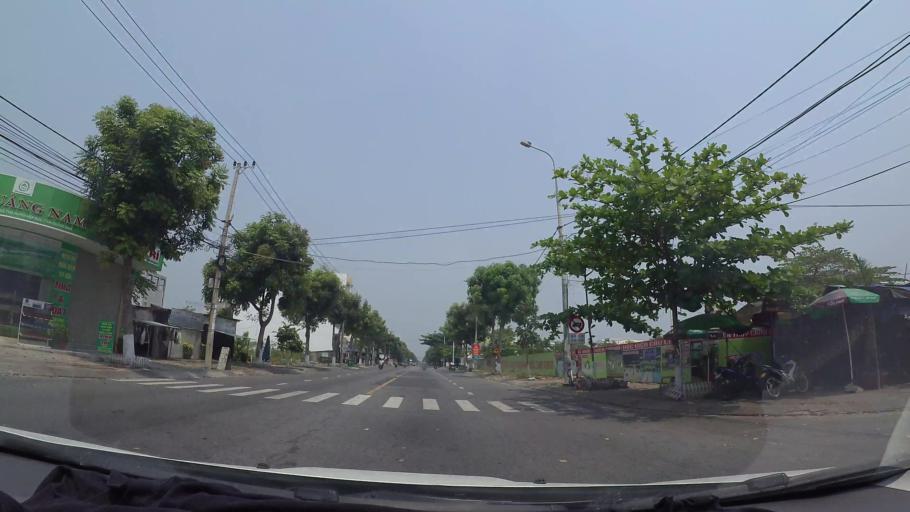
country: VN
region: Da Nang
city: Cam Le
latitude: 15.9865
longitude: 108.2079
